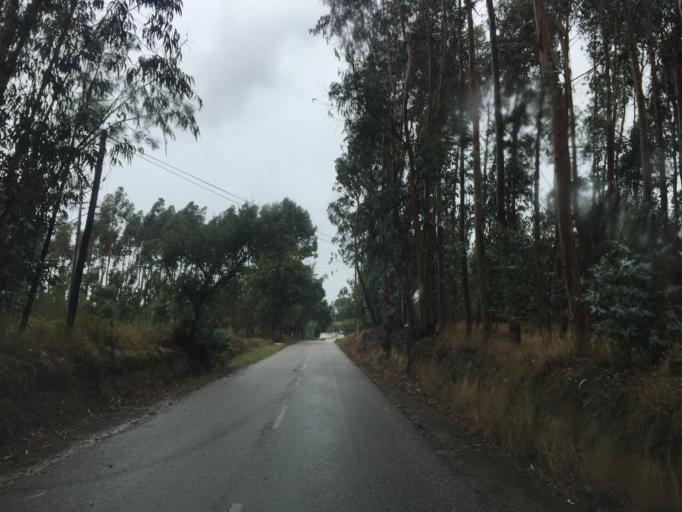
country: PT
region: Coimbra
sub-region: Figueira da Foz
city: Lavos
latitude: 40.0499
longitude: -8.7835
